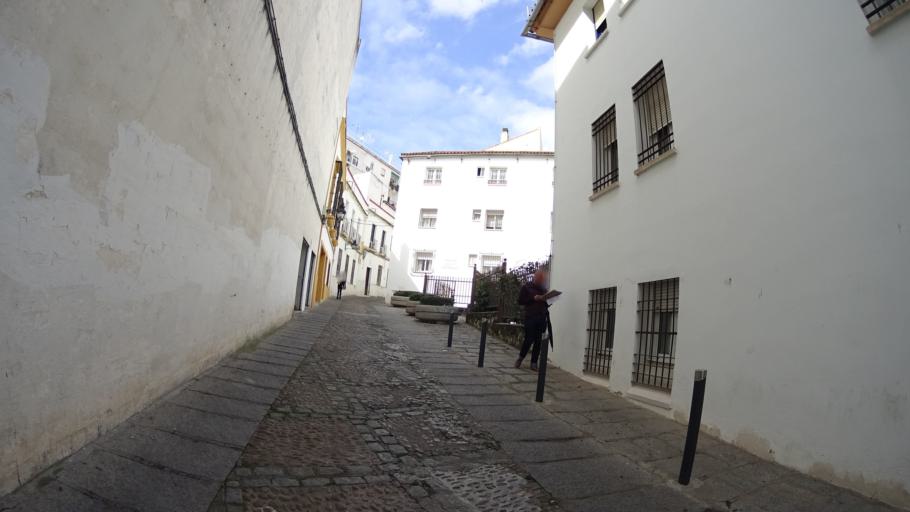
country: ES
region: Andalusia
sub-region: Province of Cordoba
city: Cordoba
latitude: 37.8890
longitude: -4.7764
